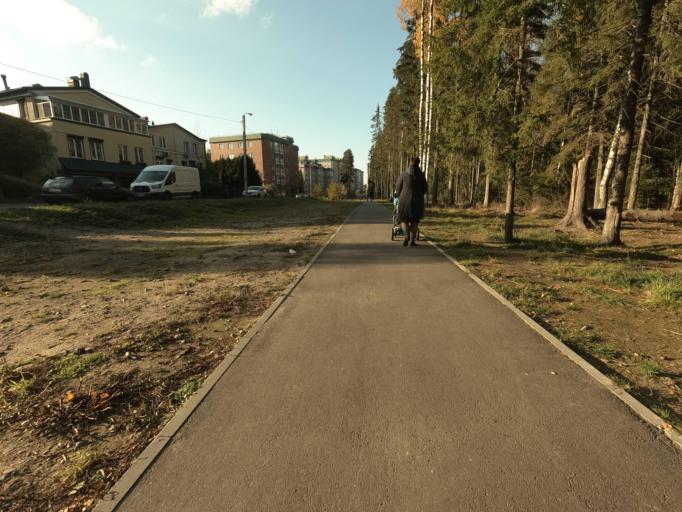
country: RU
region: Leningrad
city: Sertolovo
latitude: 60.1447
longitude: 30.2293
